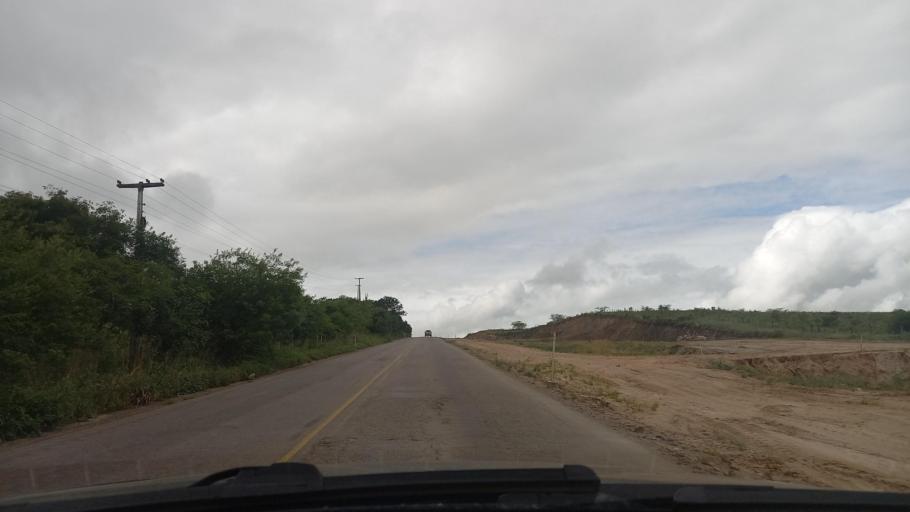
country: BR
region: Alagoas
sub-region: Batalha
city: Batalha
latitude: -9.6392
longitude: -37.1957
